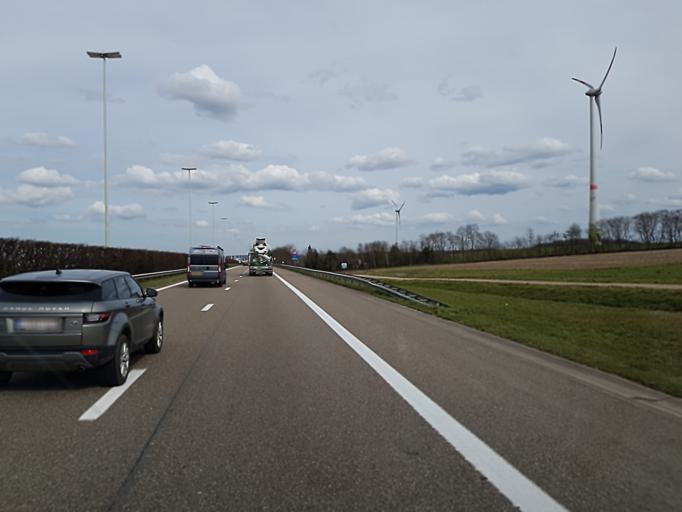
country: BE
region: Flanders
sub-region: Provincie Vlaams-Brabant
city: Diest
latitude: 50.9526
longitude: 5.0596
